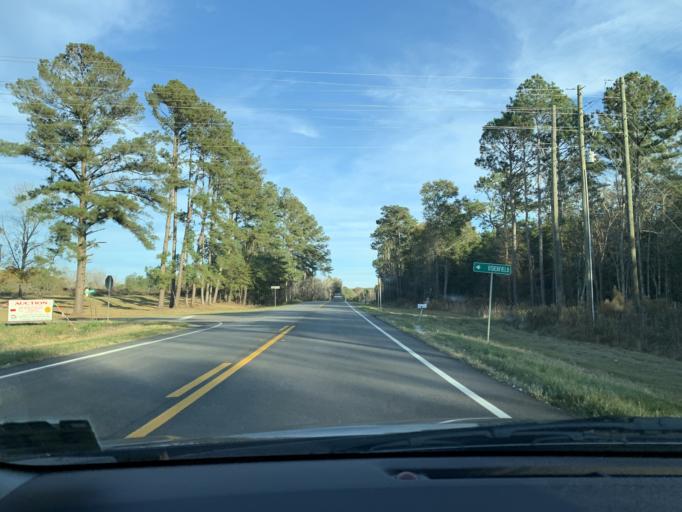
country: US
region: Georgia
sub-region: Irwin County
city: Ocilla
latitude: 31.5954
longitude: -83.1216
